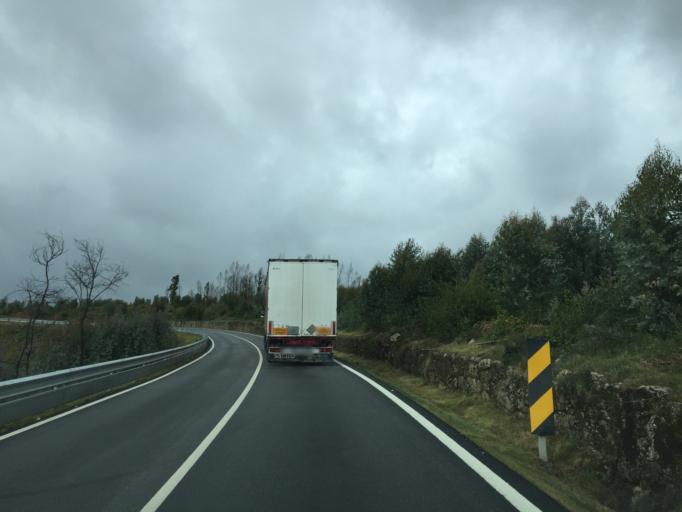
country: PT
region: Coimbra
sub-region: Oliveira do Hospital
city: Oliveira do Hospital
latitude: 40.3242
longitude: -7.9283
